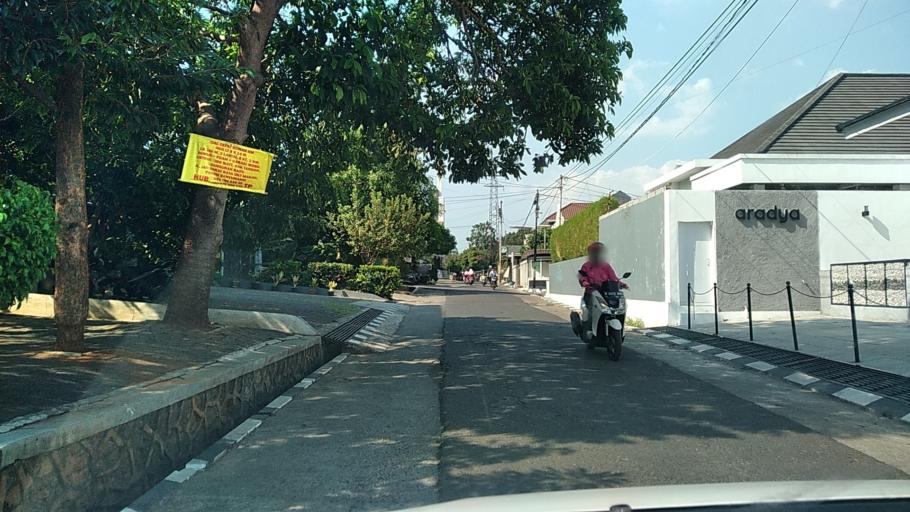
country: ID
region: Central Java
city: Semarang
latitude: -7.0647
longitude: 110.4193
